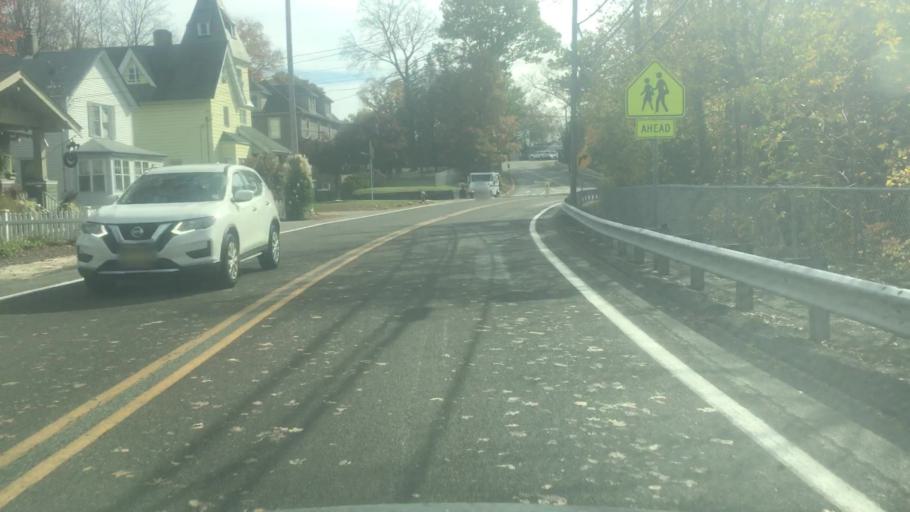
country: US
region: New Jersey
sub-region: Morris County
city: Butler
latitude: 41.0068
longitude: -74.3343
